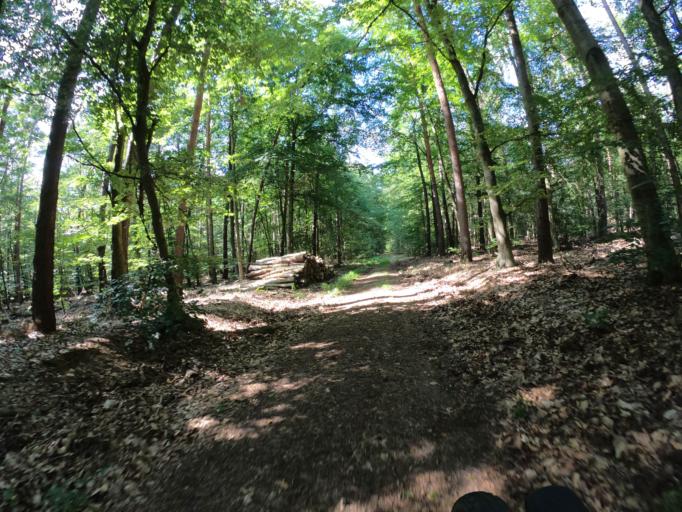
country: DE
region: Hesse
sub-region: Regierungsbezirk Darmstadt
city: Erzhausen
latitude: 49.9908
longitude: 8.6276
